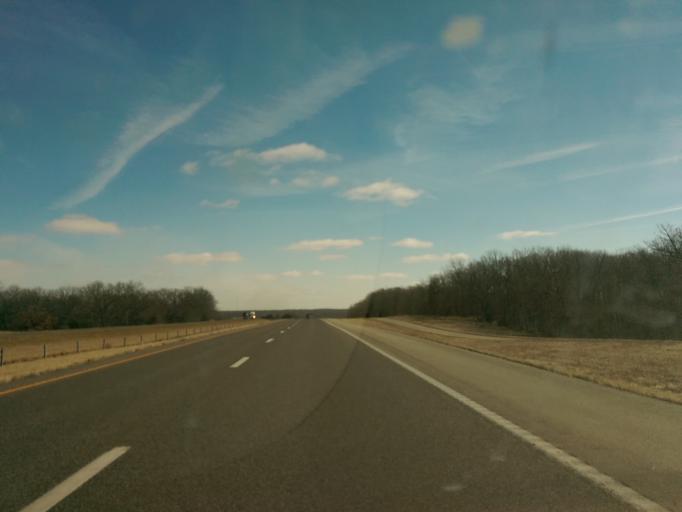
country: US
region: Missouri
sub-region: Callaway County
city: Fulton
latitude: 38.9383
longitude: -91.8614
